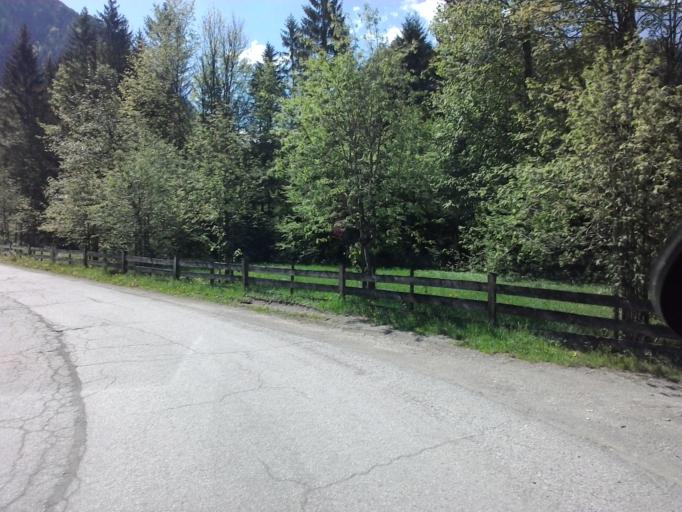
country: AT
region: Styria
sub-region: Politischer Bezirk Liezen
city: Wildalpen
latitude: 47.6666
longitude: 14.9859
